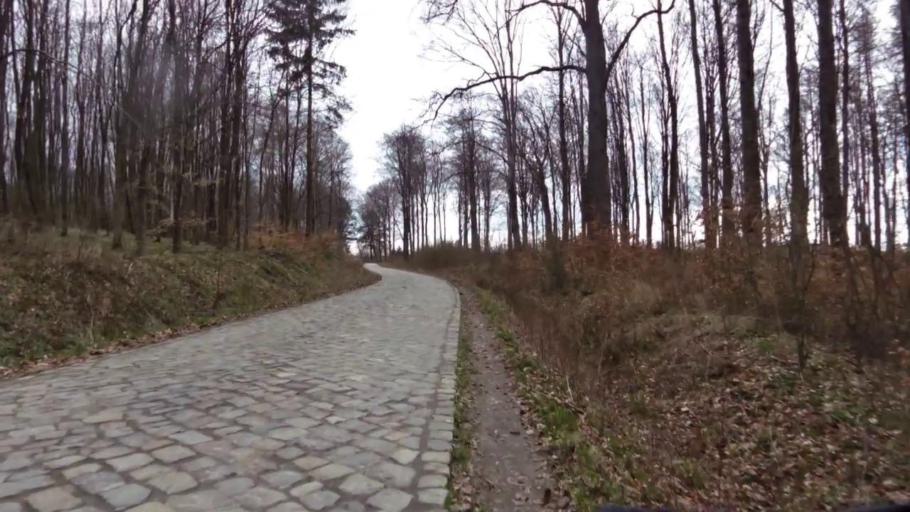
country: PL
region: West Pomeranian Voivodeship
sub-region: Powiat koszalinski
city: Sianow
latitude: 54.2715
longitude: 16.3182
